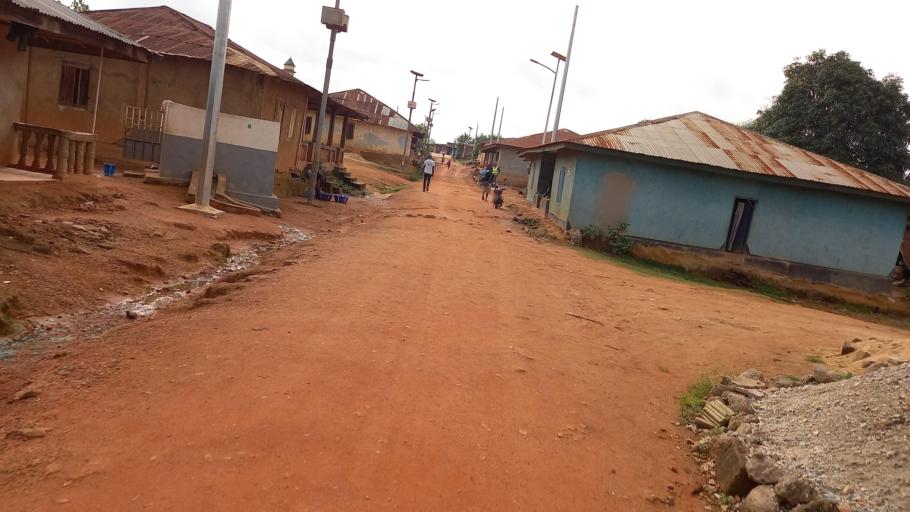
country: SL
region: Eastern Province
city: Kailahun
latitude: 8.2786
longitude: -10.5752
